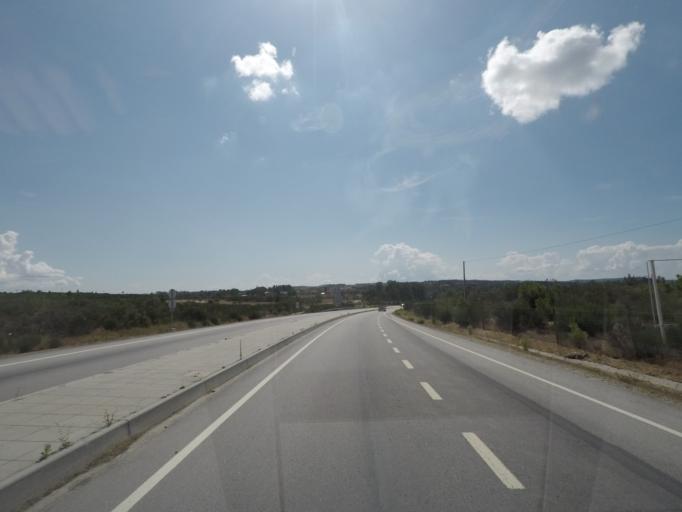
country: PT
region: Vila Real
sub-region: Murca
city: Murca
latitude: 41.3369
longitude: -7.4697
